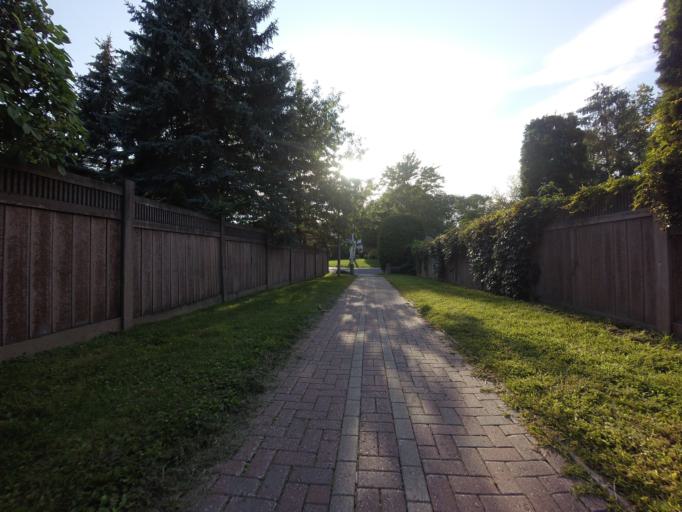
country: CA
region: Ontario
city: Bells Corners
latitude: 45.3407
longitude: -75.7750
